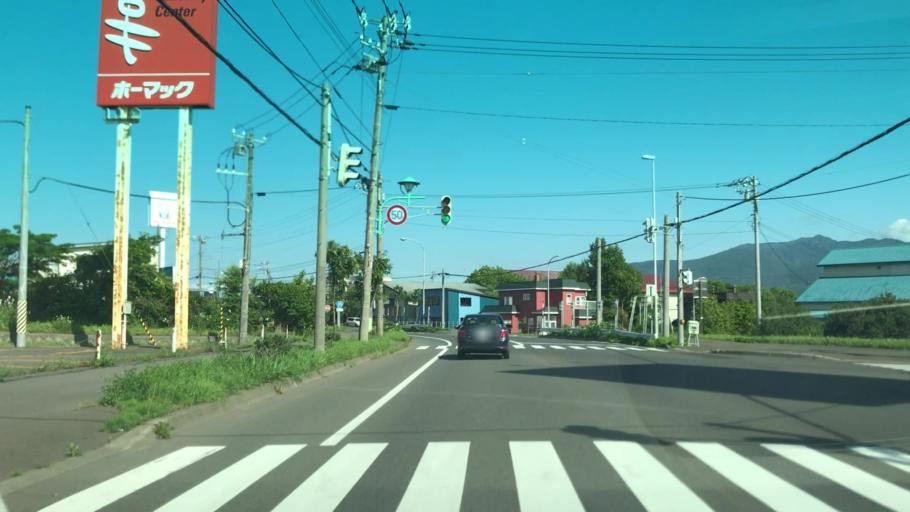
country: JP
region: Hokkaido
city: Iwanai
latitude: 42.9813
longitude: 140.5395
